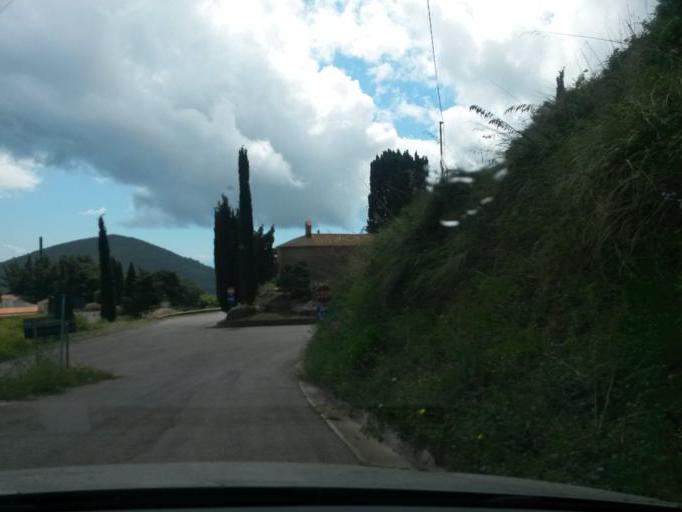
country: IT
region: Tuscany
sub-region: Provincia di Livorno
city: Rio nell'Elba
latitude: 42.8173
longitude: 10.4024
